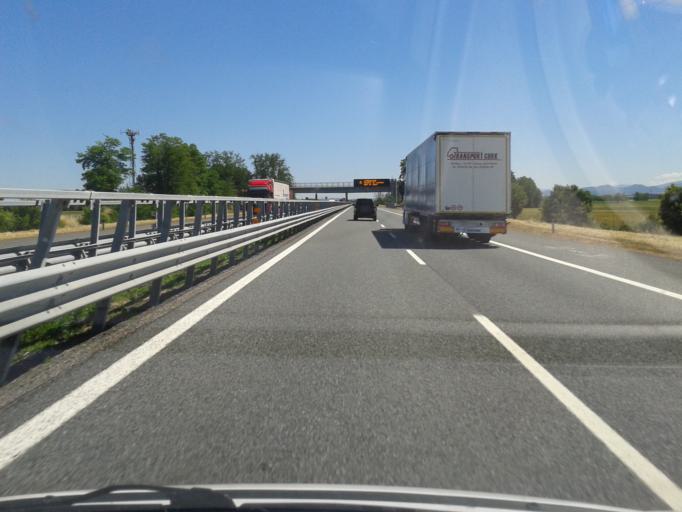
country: IT
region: Piedmont
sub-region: Provincia di Alessandria
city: Basaluzzo
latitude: 44.7806
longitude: 8.7054
